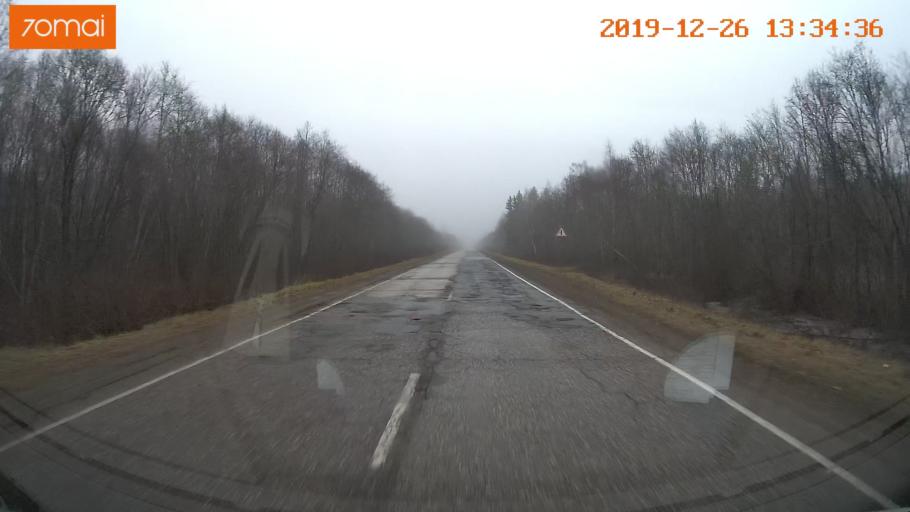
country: RU
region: Vologda
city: Sheksna
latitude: 58.8035
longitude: 38.3265
